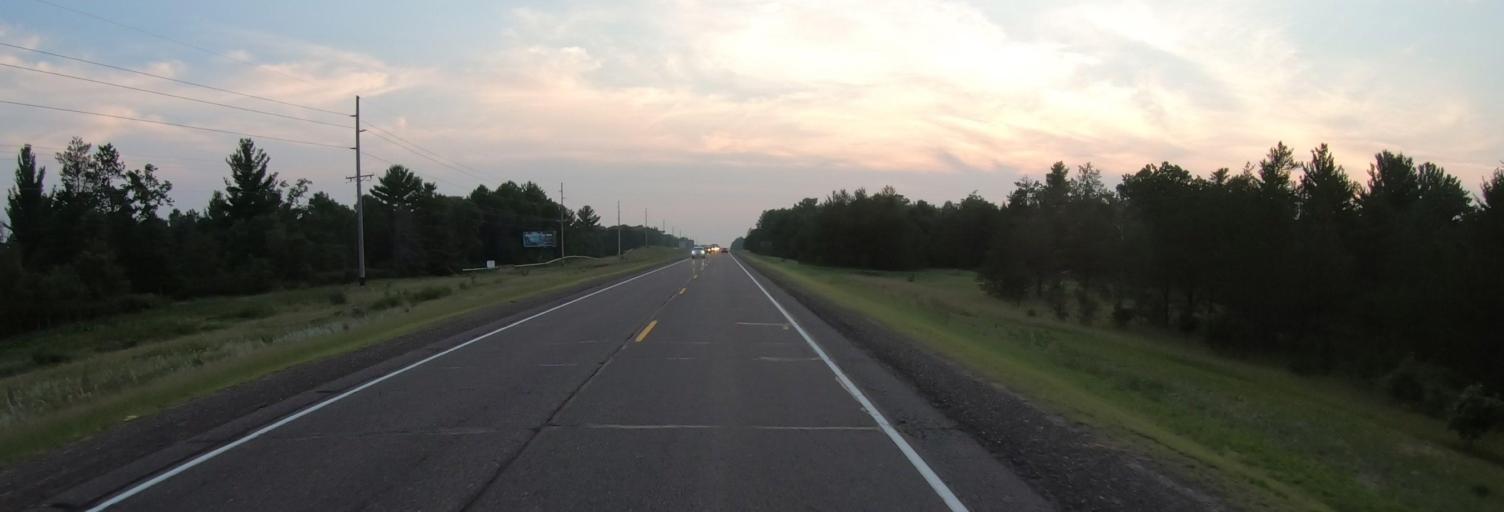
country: US
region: Wisconsin
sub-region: Burnett County
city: Grantsburg
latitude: 45.7732
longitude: -92.7379
